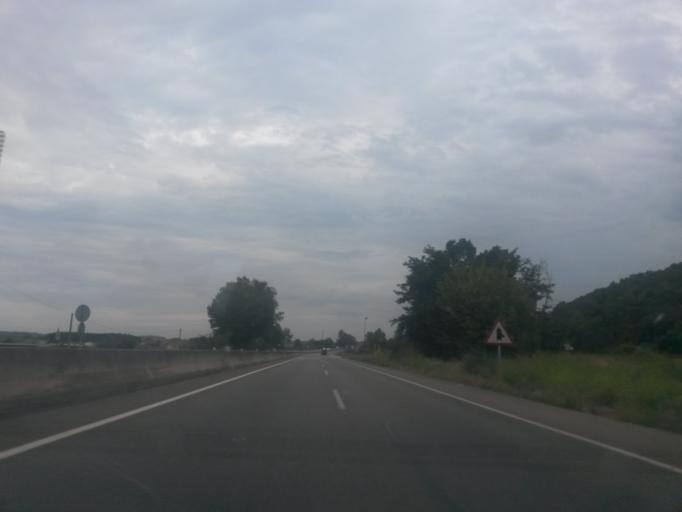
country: ES
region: Catalonia
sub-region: Provincia de Girona
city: Cornella del Terri
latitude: 42.0918
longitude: 2.8062
